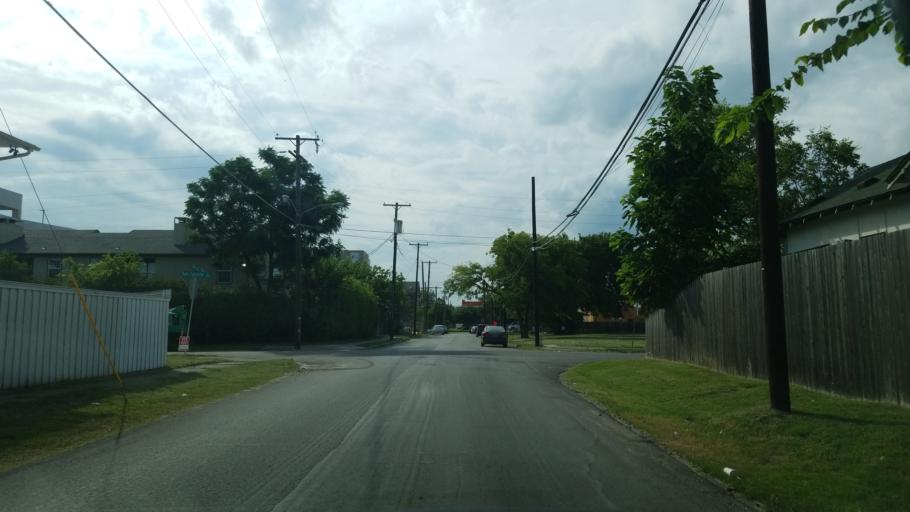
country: US
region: Texas
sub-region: Dallas County
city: Highland Park
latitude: 32.8038
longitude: -96.7764
